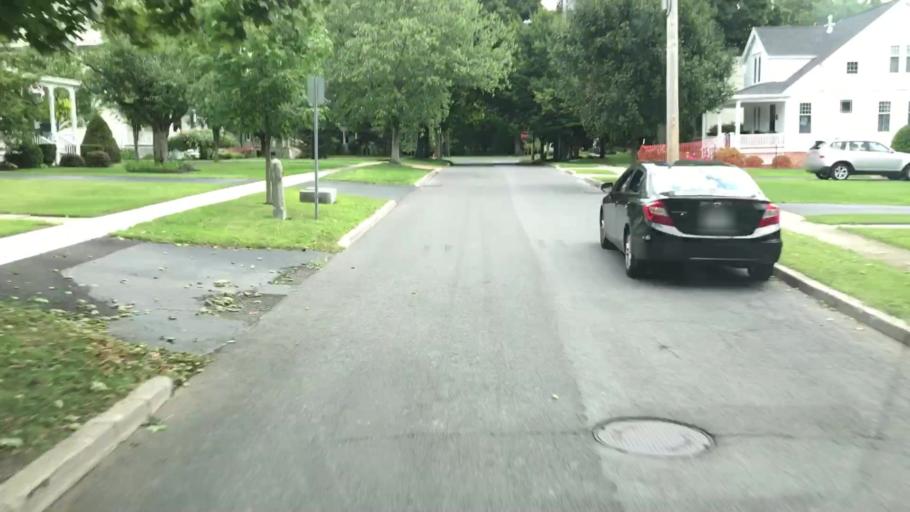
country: US
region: New York
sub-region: Onondaga County
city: Skaneateles
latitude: 42.9480
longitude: -76.4246
